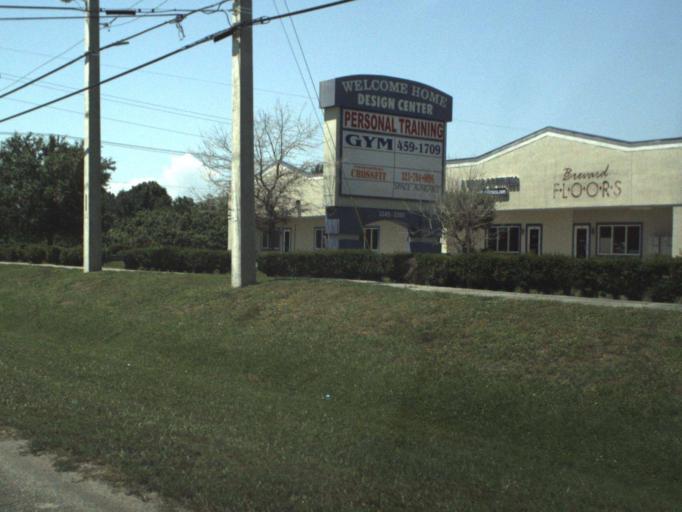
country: US
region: Florida
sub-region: Brevard County
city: Cocoa
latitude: 28.4173
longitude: -80.7068
